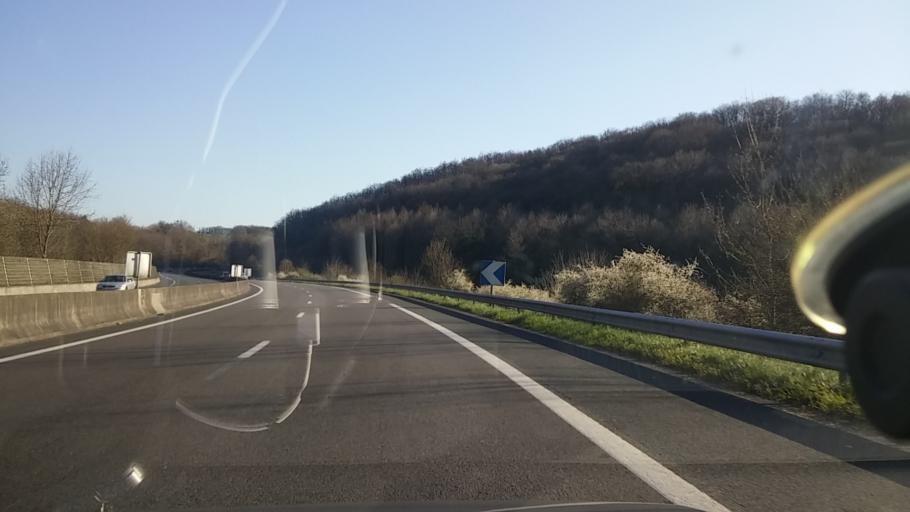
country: FR
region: Centre
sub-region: Departement de l'Indre
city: Saint-Marcel
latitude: 46.6010
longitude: 1.4982
